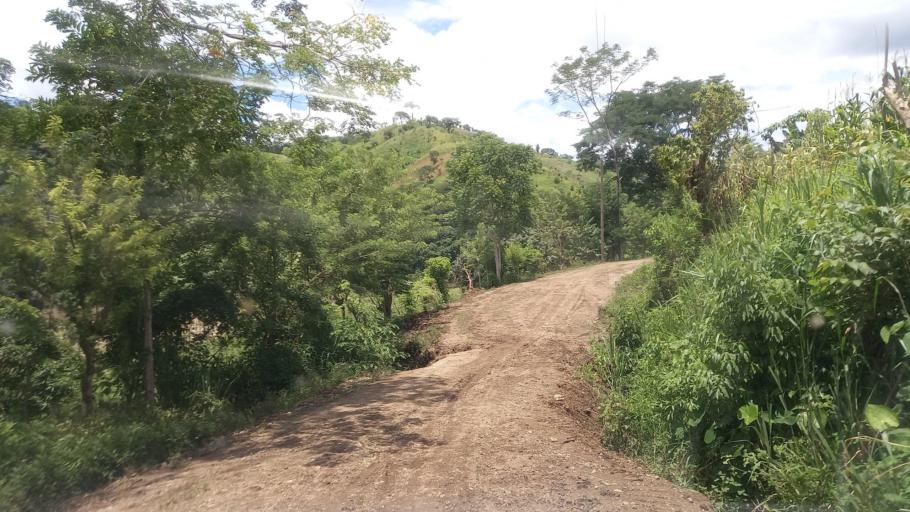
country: NI
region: Nueva Segovia
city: Wiwili
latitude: 13.7423
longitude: -85.7899
